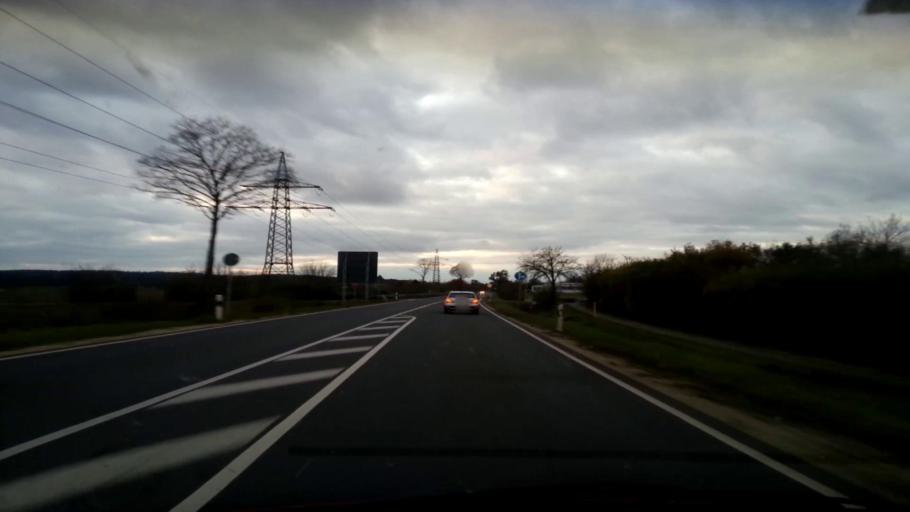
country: DE
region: Bavaria
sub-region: Upper Franconia
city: Sonnefeld
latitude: 50.2127
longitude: 11.0866
